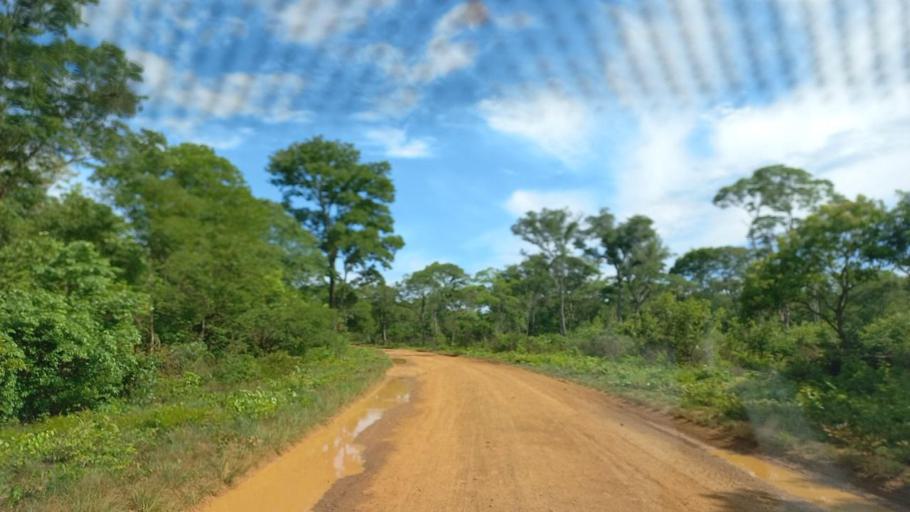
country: ZM
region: North-Western
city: Kabompo
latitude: -13.0854
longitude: 24.2204
